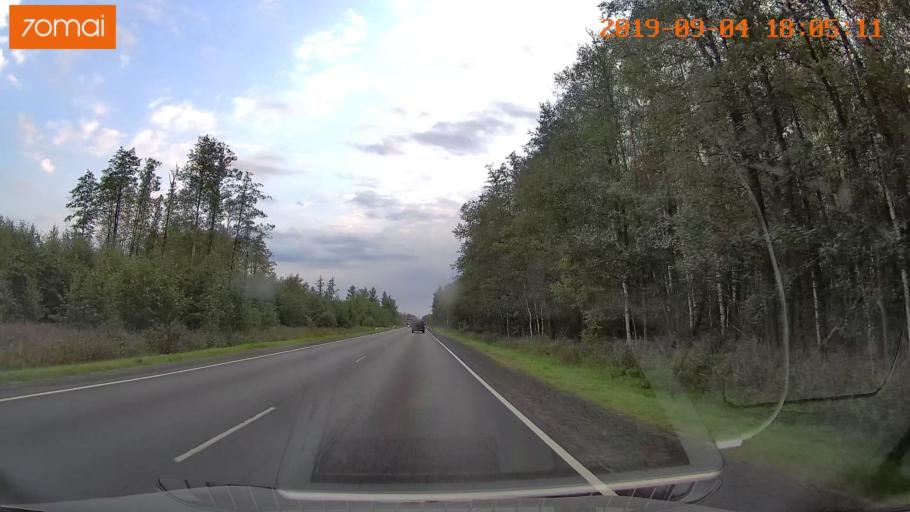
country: RU
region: Moskovskaya
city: Il'inskiy Pogost
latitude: 55.4441
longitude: 38.8297
